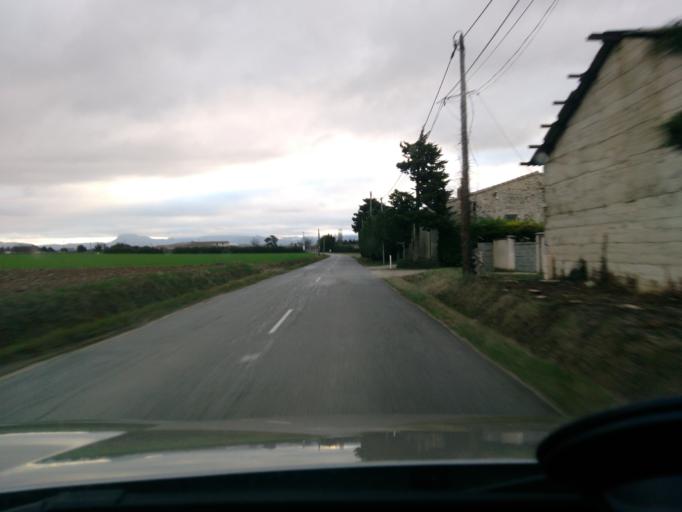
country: FR
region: Rhone-Alpes
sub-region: Departement de la Drome
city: Saint-Marcel-les-Sauzet
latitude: 44.5718
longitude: 4.8172
